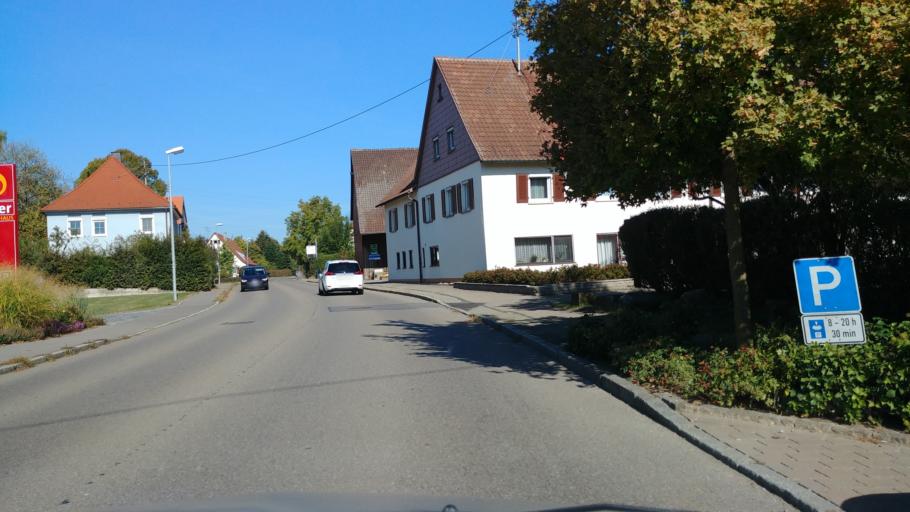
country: DE
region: Baden-Wuerttemberg
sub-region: Regierungsbezirk Stuttgart
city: Michelbach an der Bilz
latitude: 49.0693
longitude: 9.7251
